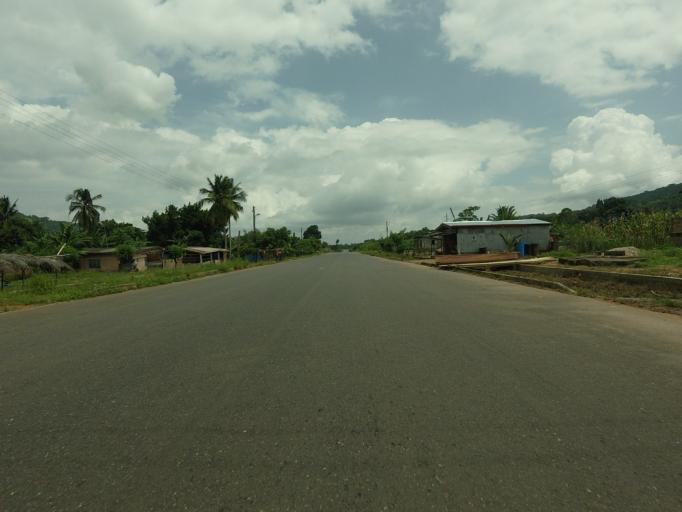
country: GH
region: Volta
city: Ho
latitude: 6.5299
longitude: 0.2267
